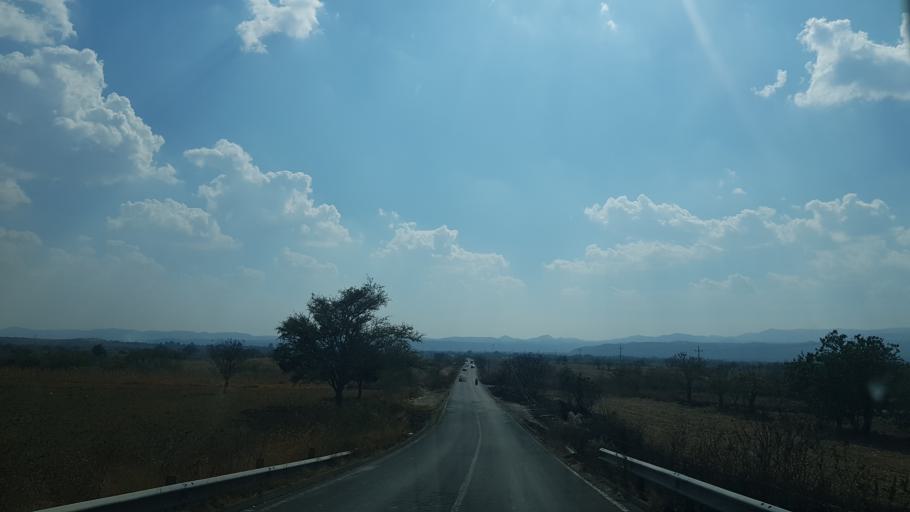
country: MX
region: Puebla
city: Atlixco
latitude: 18.9010
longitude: -98.4923
